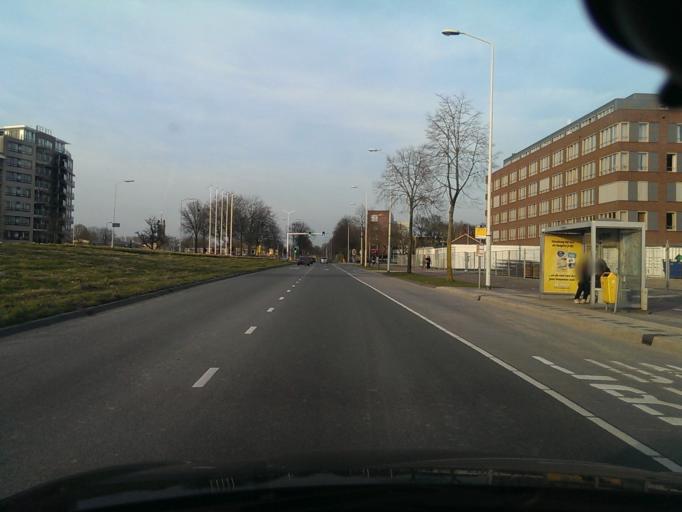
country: NL
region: North Brabant
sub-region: Gemeente Waalre
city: Waalre
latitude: 51.4196
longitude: 5.4461
